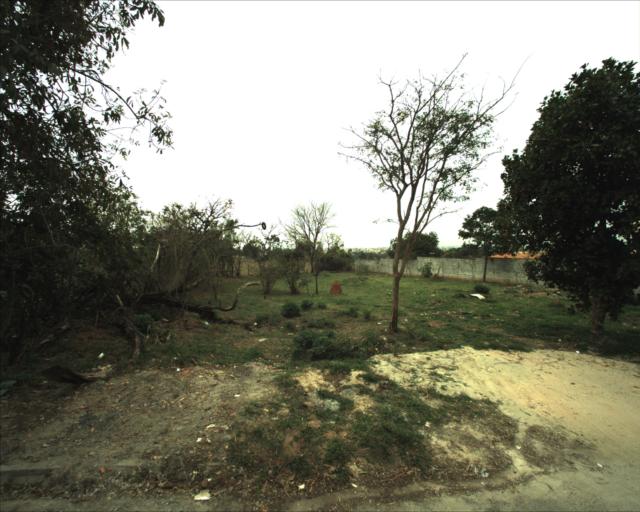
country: BR
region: Sao Paulo
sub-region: Sorocaba
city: Sorocaba
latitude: -23.4934
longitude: -47.5303
